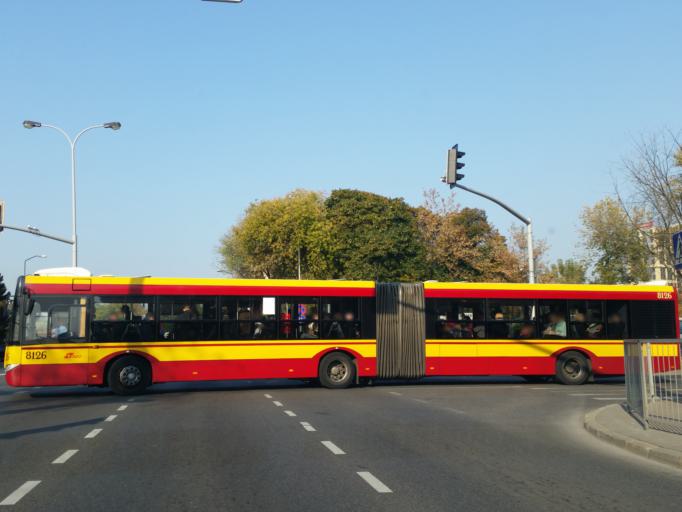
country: PL
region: Masovian Voivodeship
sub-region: Warszawa
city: Mokotow
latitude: 52.1790
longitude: 21.0249
